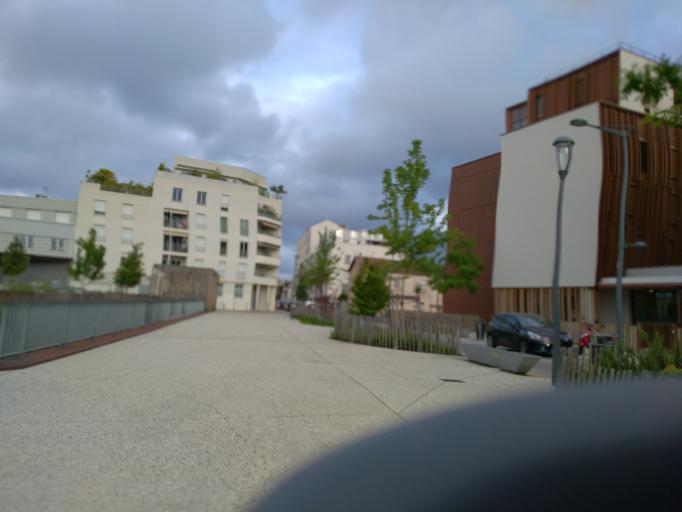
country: FR
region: Rhone-Alpes
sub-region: Departement du Rhone
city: Villeurbanne
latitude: 45.7478
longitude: 4.8768
